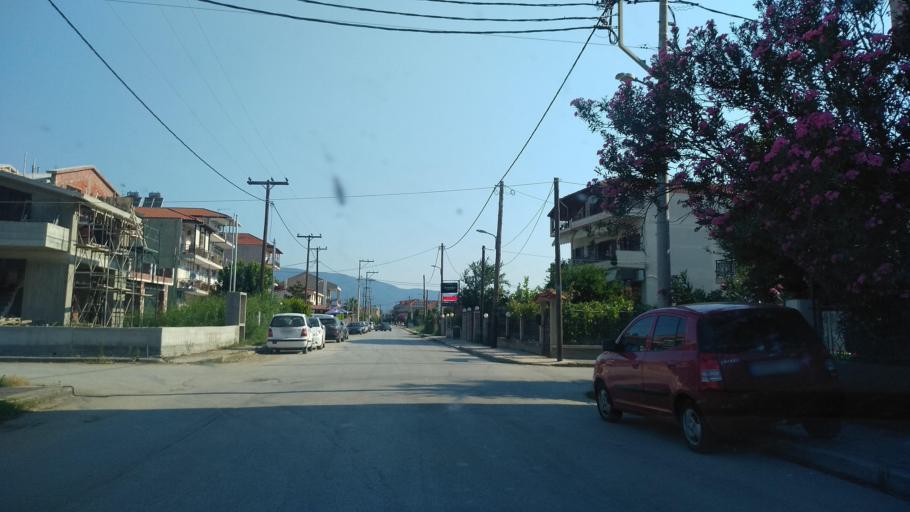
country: GR
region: Central Macedonia
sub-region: Nomos Thessalonikis
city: Stavros
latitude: 40.6678
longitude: 23.6912
